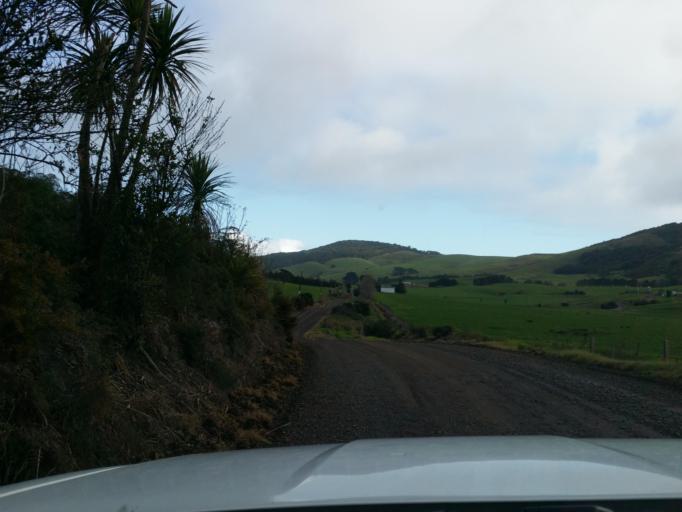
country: NZ
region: Northland
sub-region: Kaipara District
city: Dargaville
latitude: -35.7490
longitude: 173.5836
